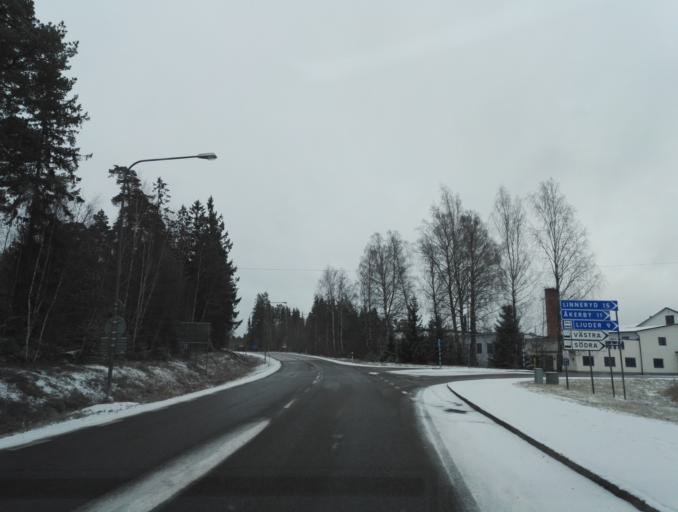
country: SE
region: Kronoberg
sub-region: Lessebo Kommun
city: Lessebo
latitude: 56.7442
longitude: 15.2692
